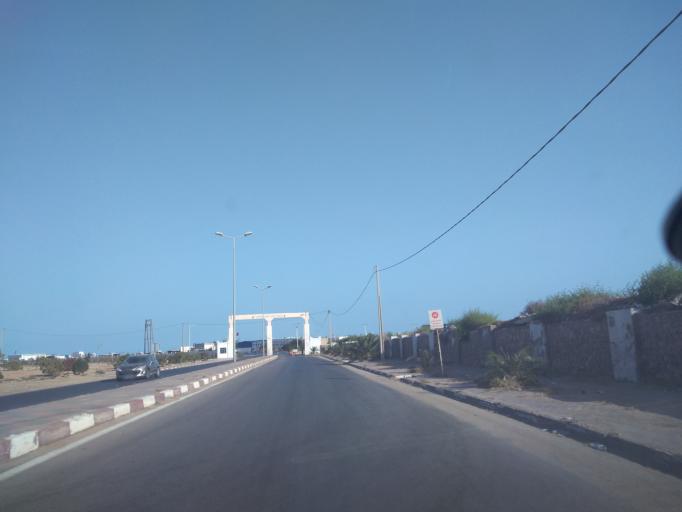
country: TN
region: Safaqis
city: Sfax
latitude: 34.7224
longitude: 10.7596
